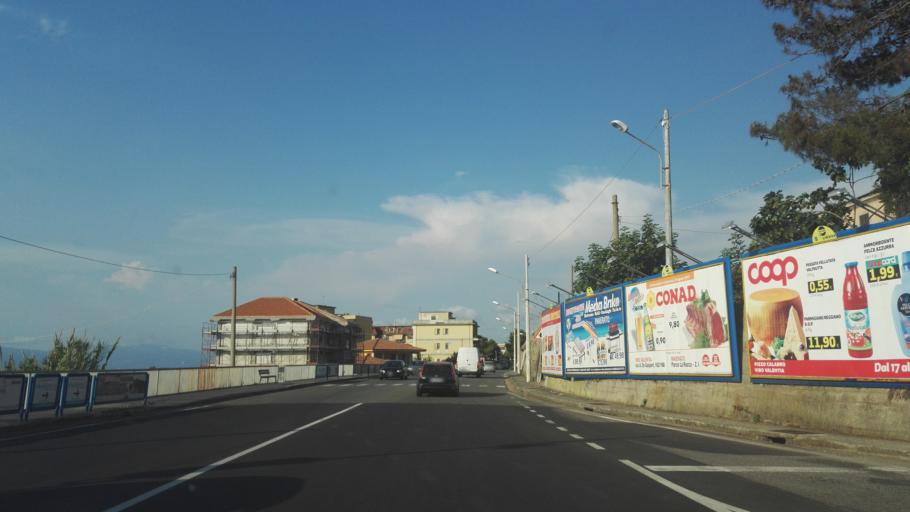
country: IT
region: Calabria
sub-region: Provincia di Vibo-Valentia
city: Maierato
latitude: 38.7324
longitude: 16.1610
